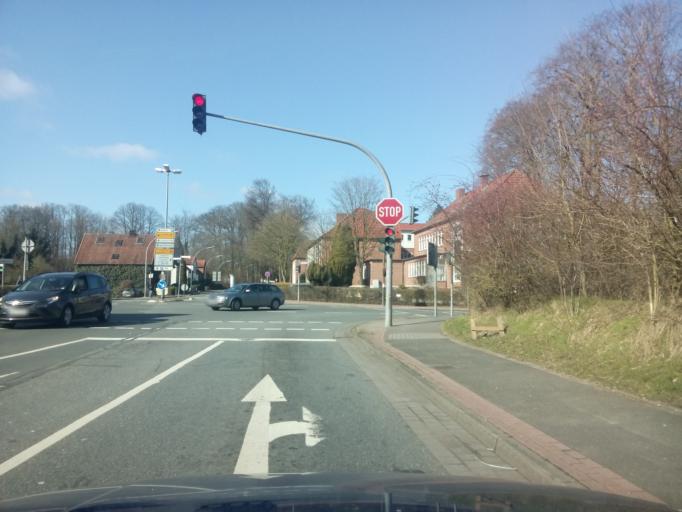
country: DE
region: Lower Saxony
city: Osterholz-Scharmbeck
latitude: 53.2206
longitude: 8.8029
